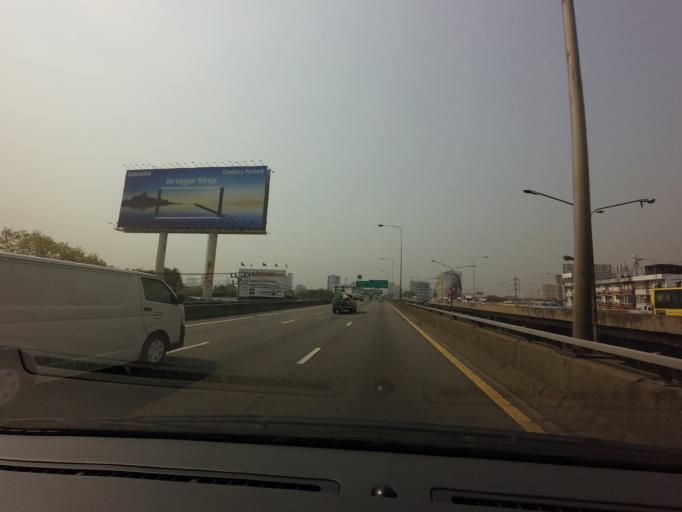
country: TH
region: Bangkok
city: Yan Nawa
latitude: 13.7099
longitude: 100.5513
